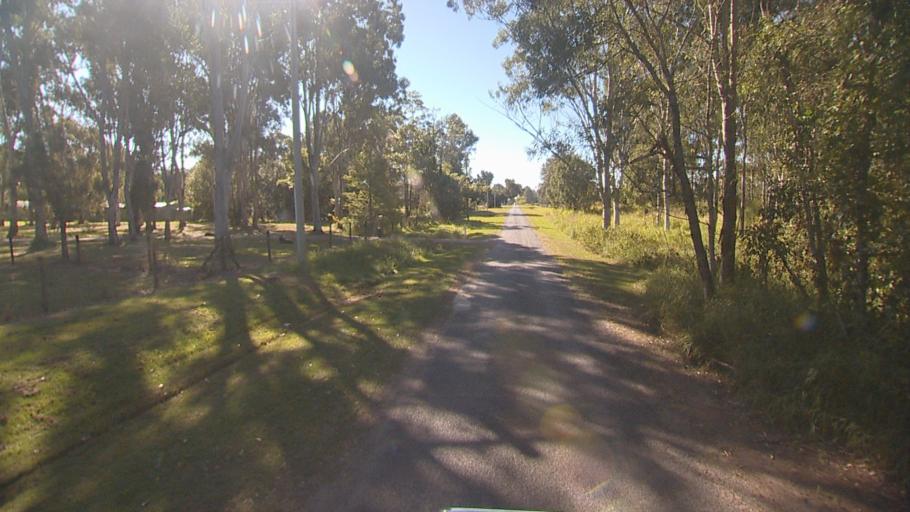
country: AU
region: Queensland
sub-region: Logan
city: Waterford West
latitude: -27.7202
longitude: 153.1258
